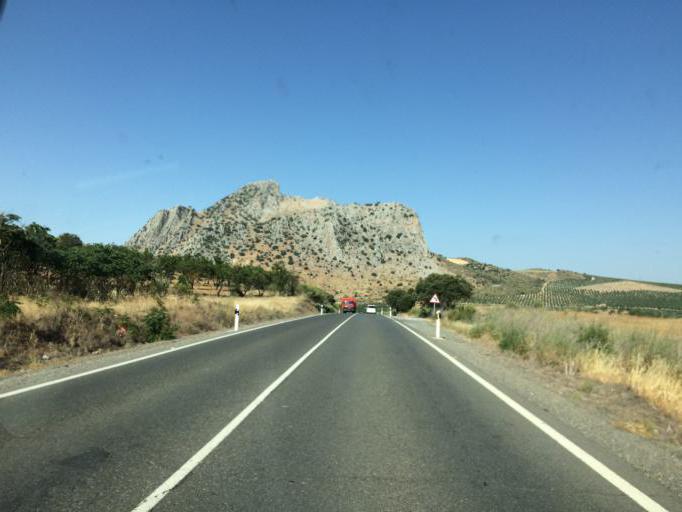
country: ES
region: Andalusia
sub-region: Provincia de Malaga
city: Archidona
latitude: 37.0774
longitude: -4.4720
